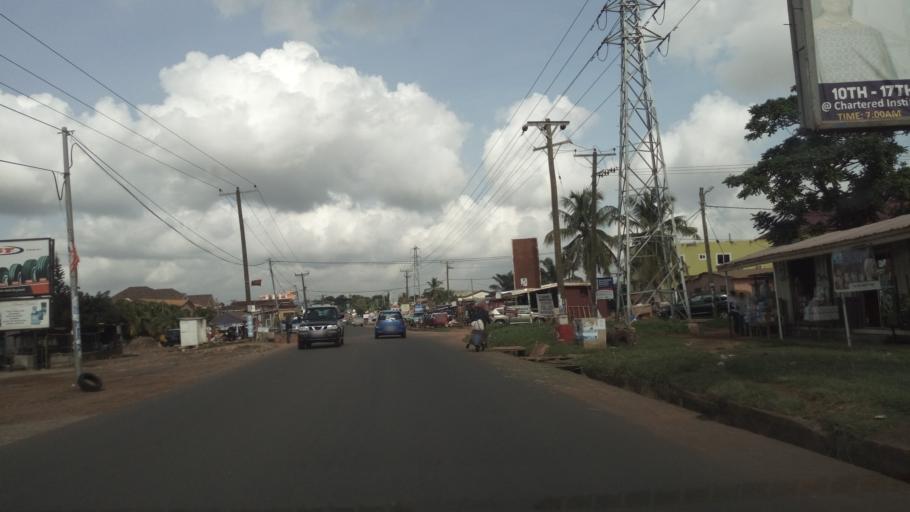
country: GH
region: Greater Accra
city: Medina Estates
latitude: 5.6599
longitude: -0.1554
